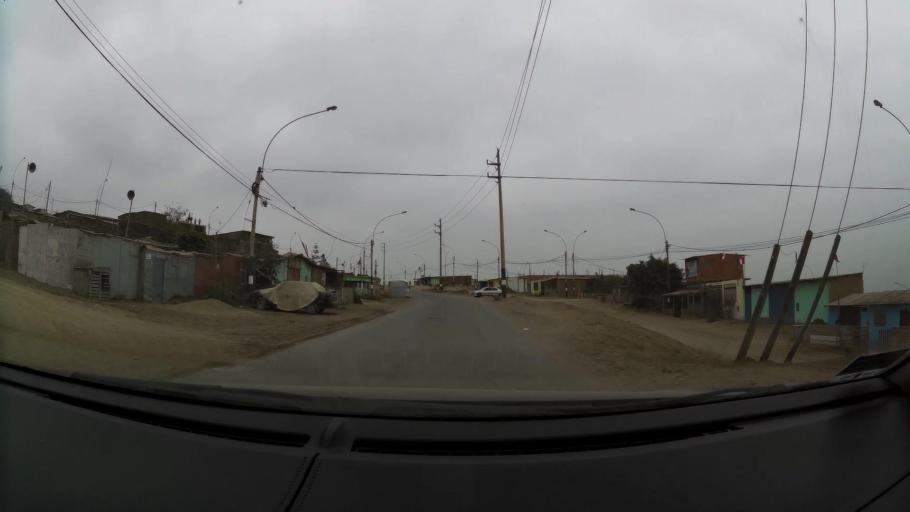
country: PE
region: Lima
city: Ventanilla
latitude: -11.8509
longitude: -77.1455
